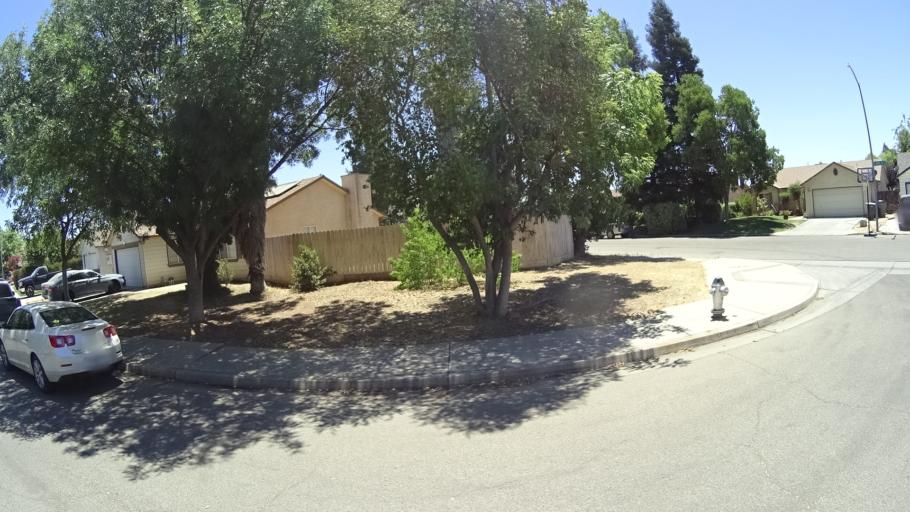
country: US
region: California
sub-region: Fresno County
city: Fresno
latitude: 36.7916
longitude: -119.8140
